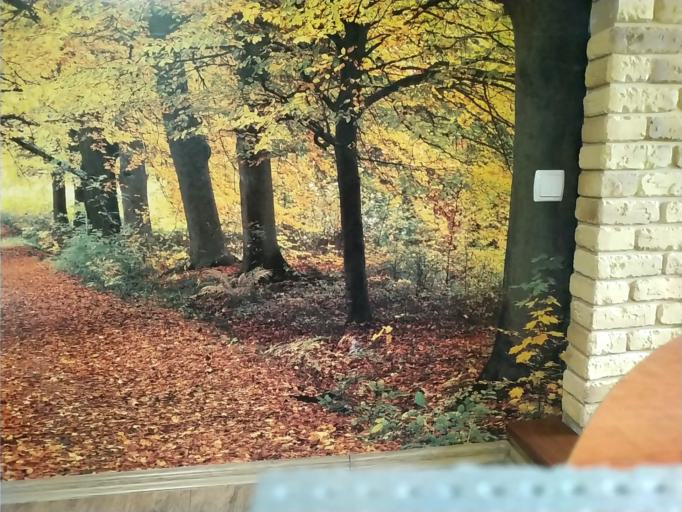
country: RU
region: Moskovskaya
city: Mikulino
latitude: 56.4857
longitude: 35.2856
